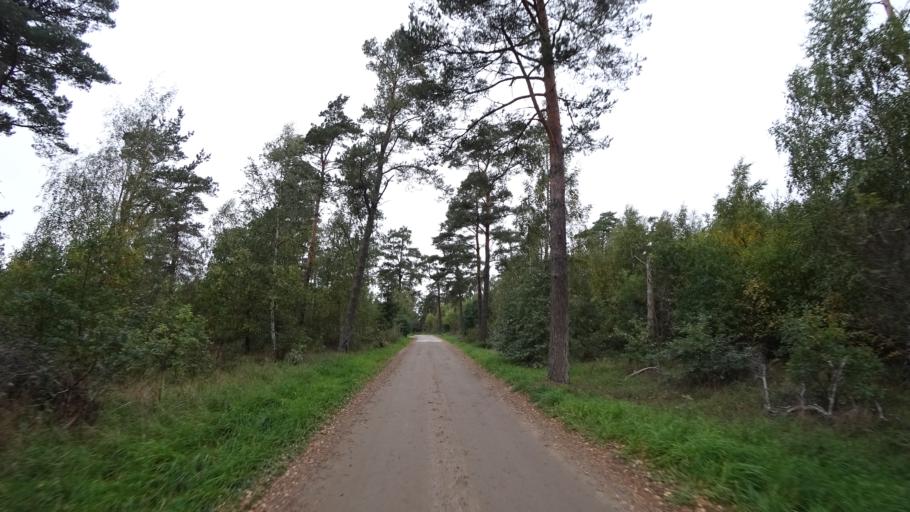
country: SE
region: Skane
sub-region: Kavlinge Kommun
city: Hofterup
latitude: 55.8243
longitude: 12.9500
